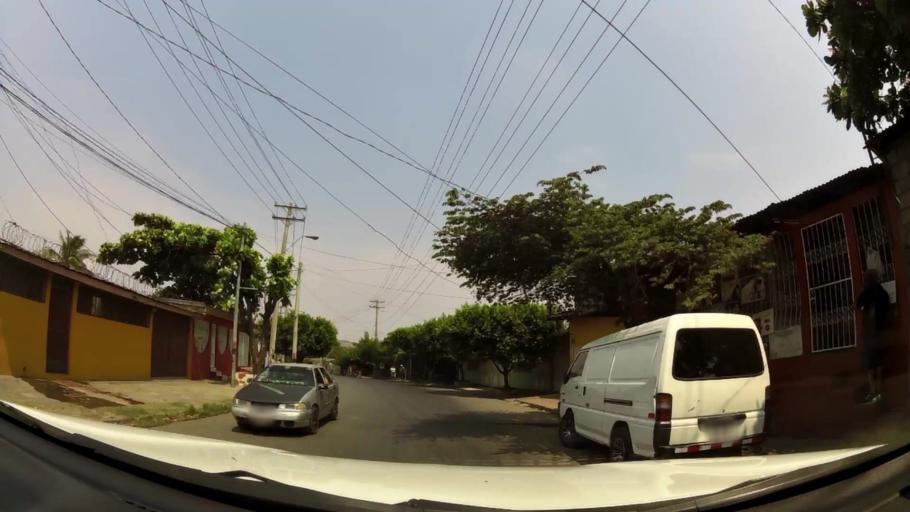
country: NI
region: Managua
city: Ciudad Sandino
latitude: 12.1590
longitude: -86.3052
